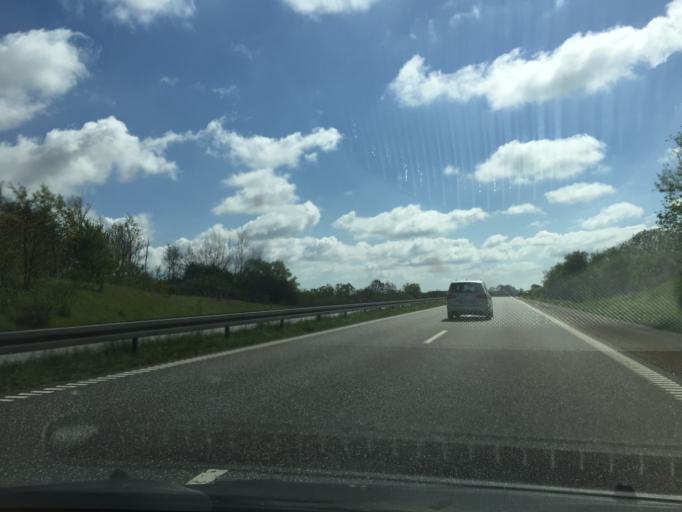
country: DK
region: Zealand
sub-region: Guldborgsund Kommune
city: Norre Alslev
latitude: 54.8975
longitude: 11.9214
